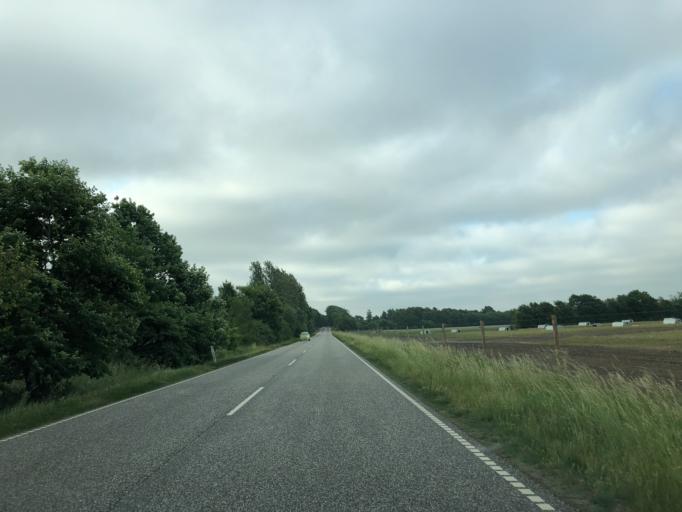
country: DK
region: South Denmark
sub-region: Vejle Kommune
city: Give
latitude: 55.8716
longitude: 9.2368
